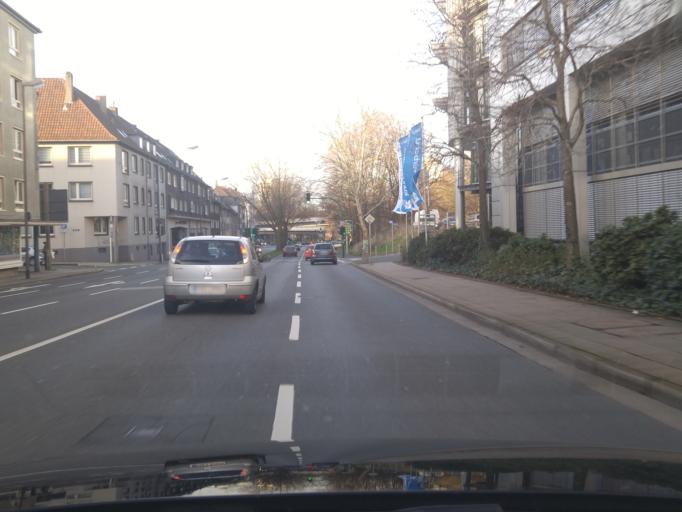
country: DE
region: North Rhine-Westphalia
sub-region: Regierungsbezirk Dusseldorf
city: Essen
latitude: 51.4475
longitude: 7.0200
